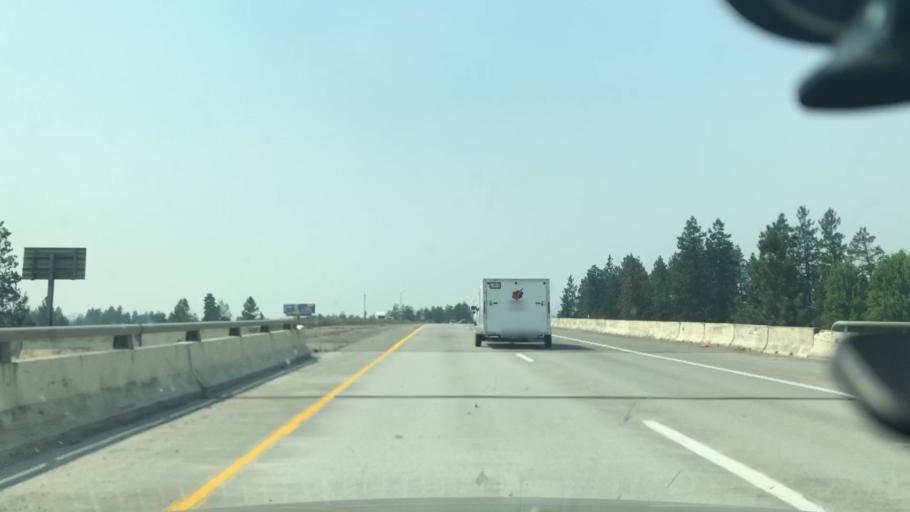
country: US
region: Idaho
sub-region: Kootenai County
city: Post Falls
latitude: 47.7127
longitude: -116.9483
